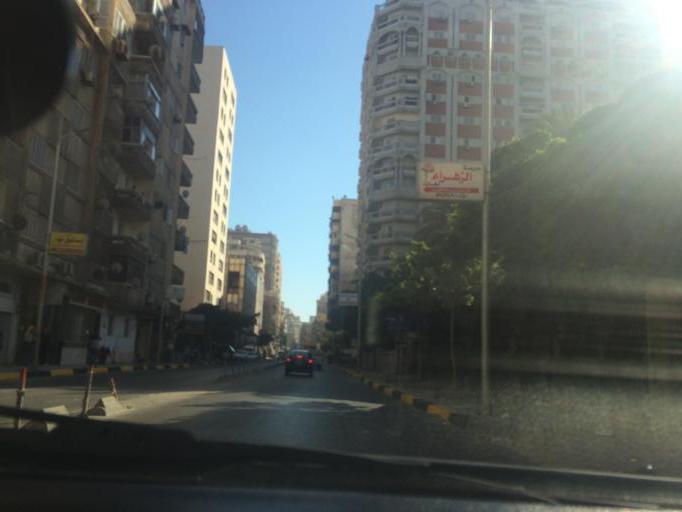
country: EG
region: Alexandria
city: Alexandria
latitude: 31.2439
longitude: 29.9708
